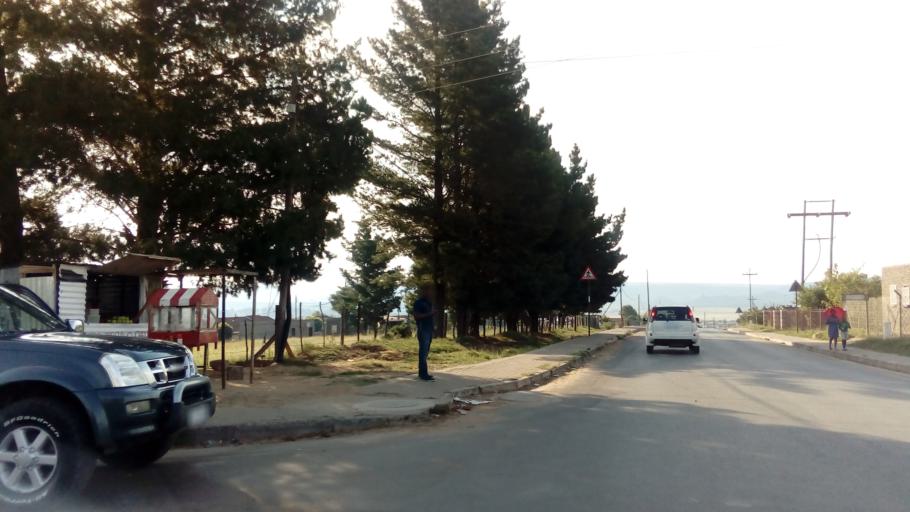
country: LS
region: Maseru
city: Maseru
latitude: -29.2918
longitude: 27.5287
